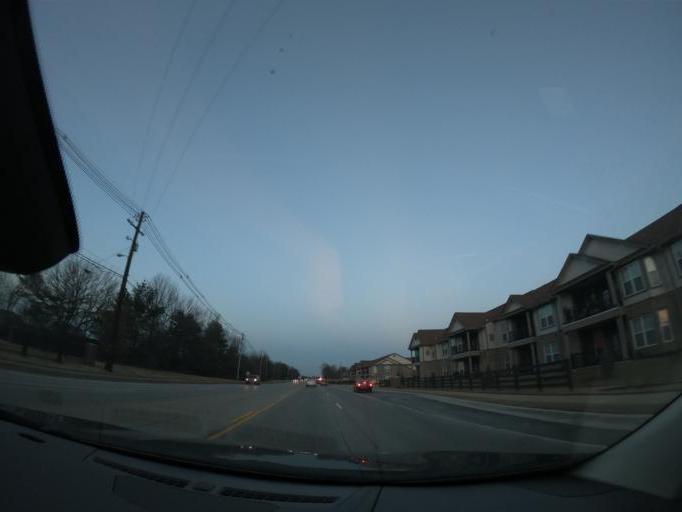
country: US
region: Kentucky
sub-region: Jefferson County
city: Worthington
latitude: 38.2900
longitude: -85.5670
